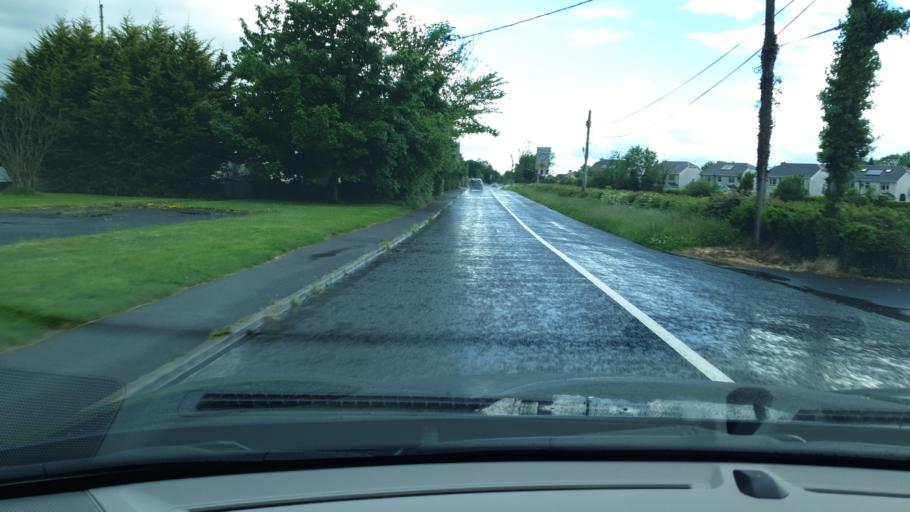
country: IE
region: Connaught
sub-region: County Galway
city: Ballinasloe
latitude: 53.3213
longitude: -8.1861
